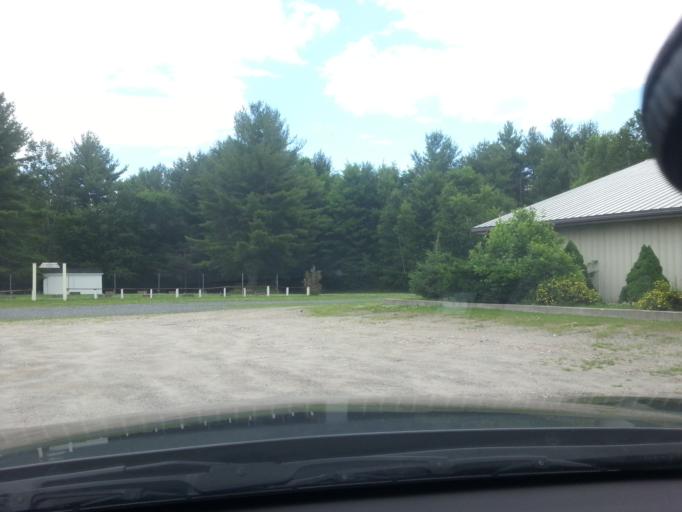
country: CA
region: Ontario
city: Gananoque
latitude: 44.6113
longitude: -76.2148
